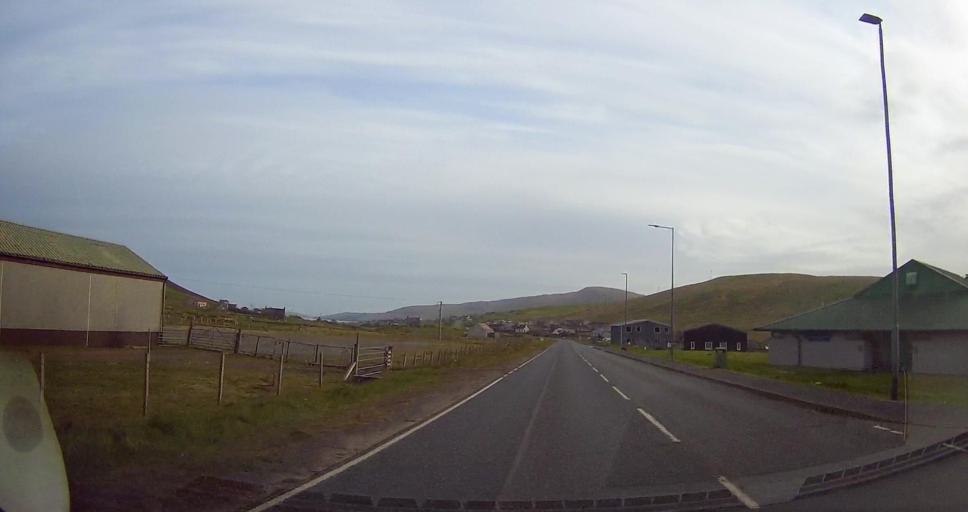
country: GB
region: Scotland
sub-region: Shetland Islands
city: Sandwick
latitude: 60.0589
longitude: -1.2231
